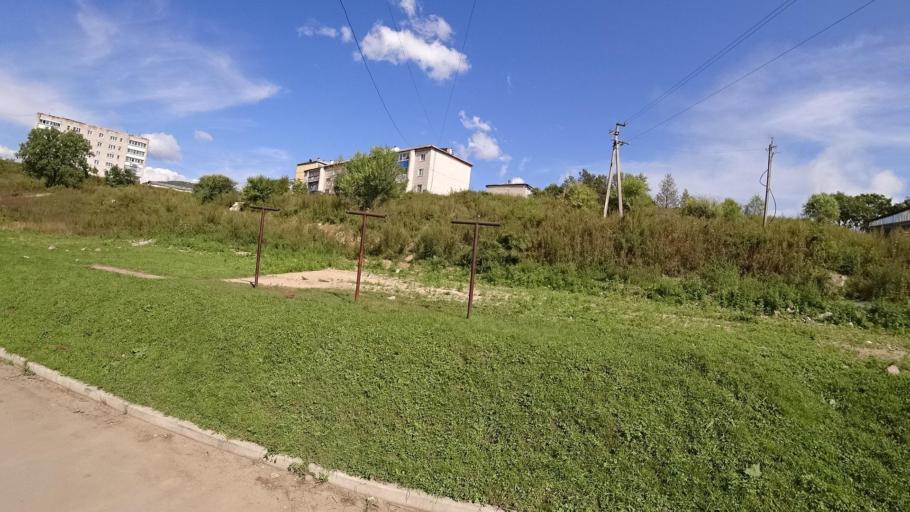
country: RU
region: Jewish Autonomous Oblast
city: Londoko
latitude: 49.0142
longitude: 131.8819
